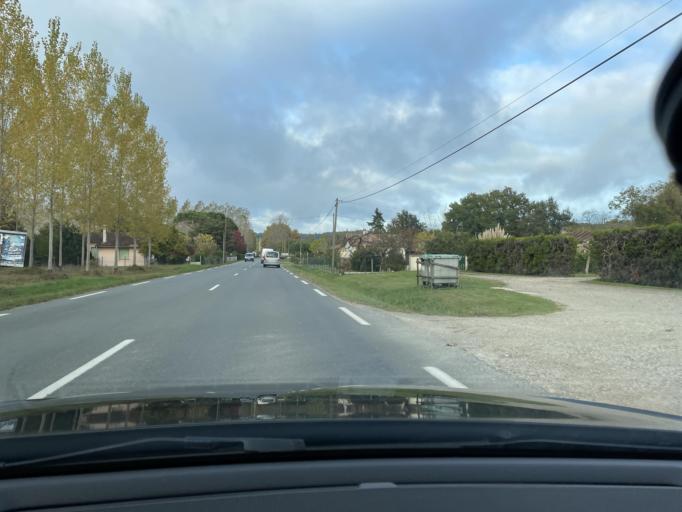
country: FR
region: Aquitaine
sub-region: Departement du Lot-et-Garonne
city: Casteljaloux
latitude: 44.3337
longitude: 0.1013
